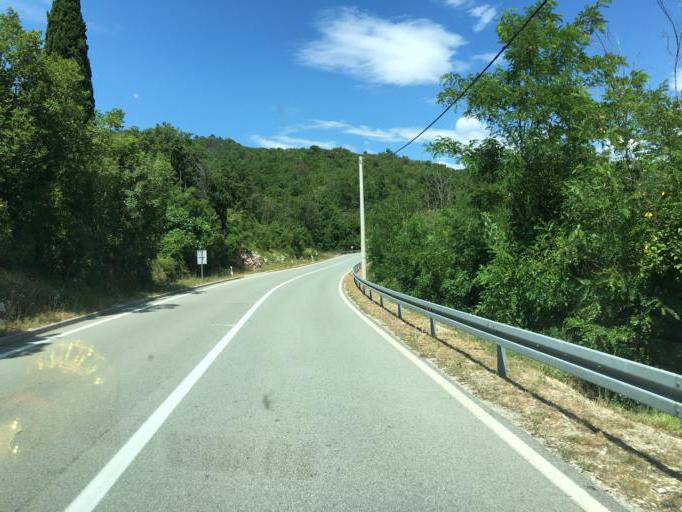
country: HR
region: Istarska
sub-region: Grad Labin
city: Rabac
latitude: 45.1617
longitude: 14.2198
